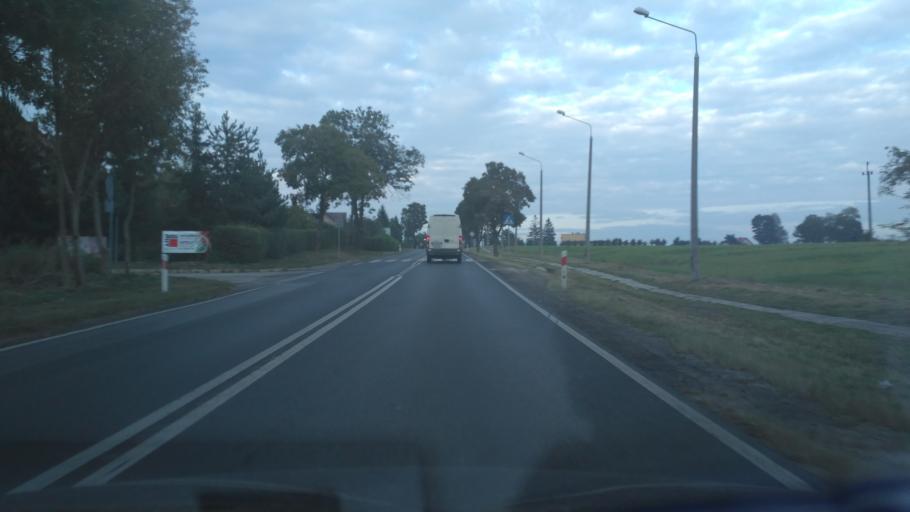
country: PL
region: Lublin Voivodeship
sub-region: Powiat lubelski
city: Jakubowice Murowane
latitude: 51.2845
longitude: 22.6724
